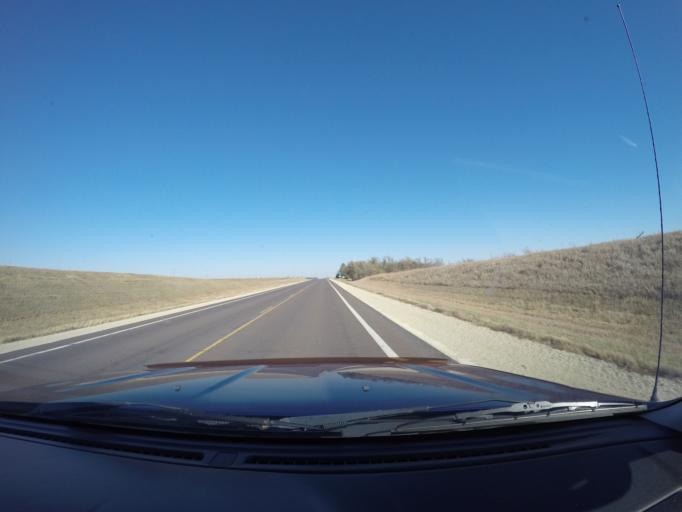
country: US
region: Kansas
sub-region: Marshall County
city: Blue Rapids
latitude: 39.6557
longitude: -96.7505
